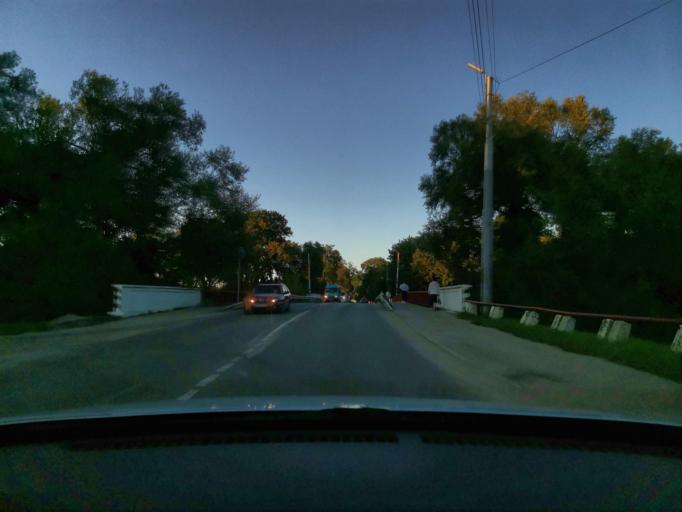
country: RU
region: Kaliningrad
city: Chernyakhovsk
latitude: 54.6424
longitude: 21.8080
